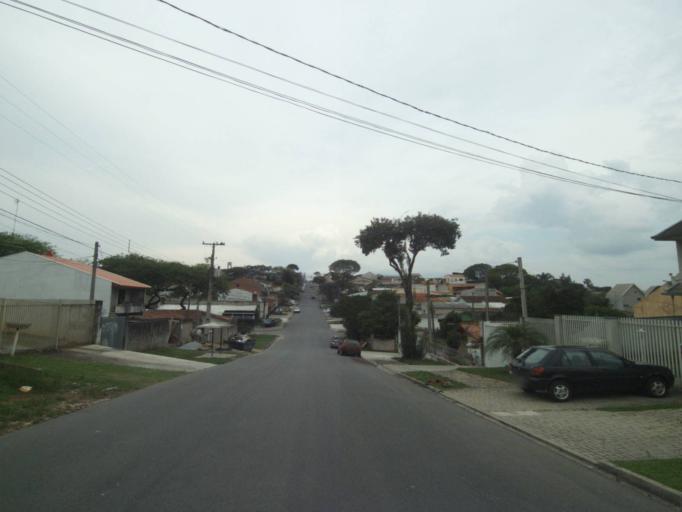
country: BR
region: Parana
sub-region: Pinhais
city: Pinhais
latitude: -25.4018
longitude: -49.2108
